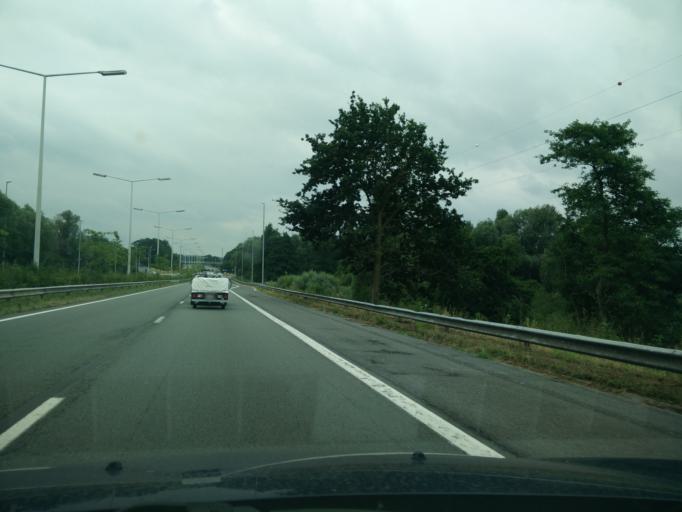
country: BE
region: Flanders
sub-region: Provincie Oost-Vlaanderen
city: Oudenaarde
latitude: 50.8452
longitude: 3.5937
